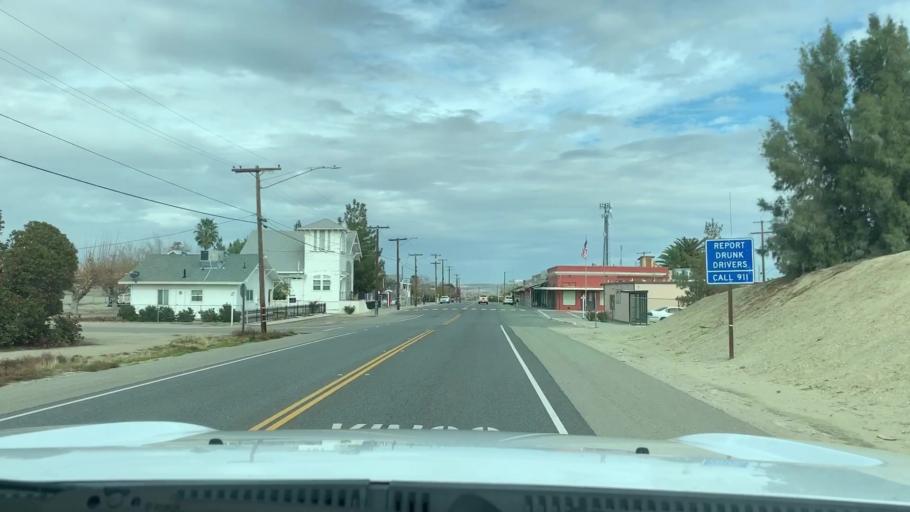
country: US
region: California
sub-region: Kern County
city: Maricopa
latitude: 35.0618
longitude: -119.4017
